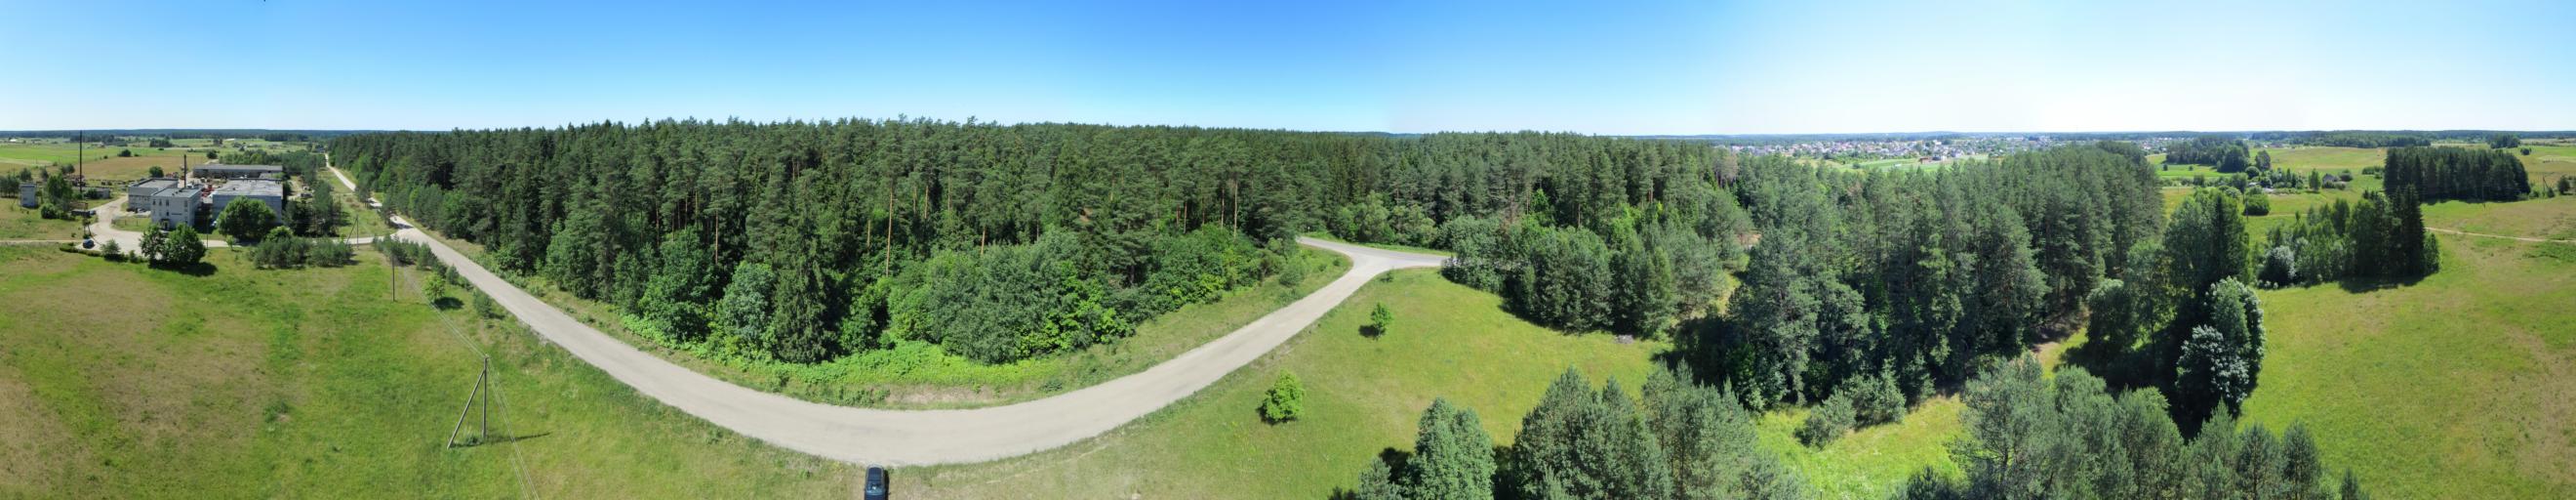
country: LT
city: Trakai
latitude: 54.6216
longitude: 24.8854
